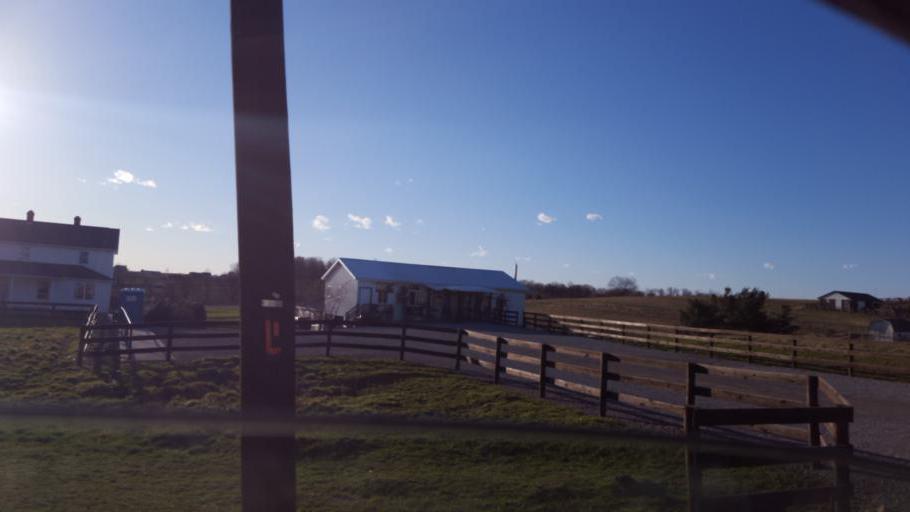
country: US
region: Ohio
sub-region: Wayne County
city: Apple Creek
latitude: 40.6404
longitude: -81.7650
